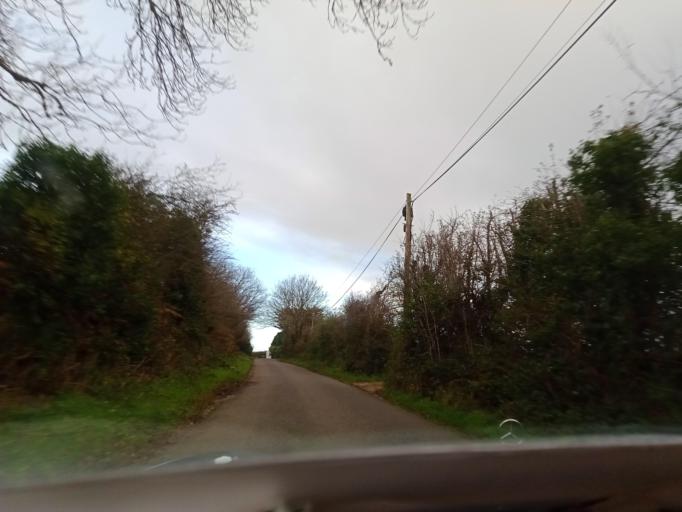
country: IE
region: Munster
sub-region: Waterford
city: Waterford
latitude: 52.3155
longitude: -7.0463
